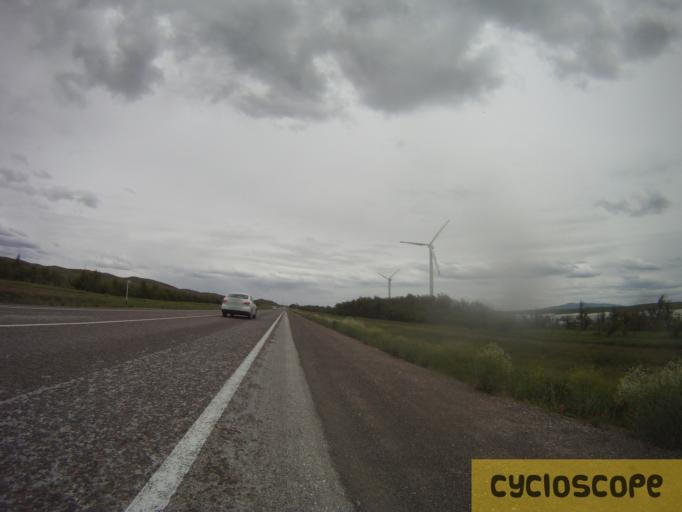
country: KZ
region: Zhambyl
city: Georgiyevka
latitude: 43.3403
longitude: 74.9661
